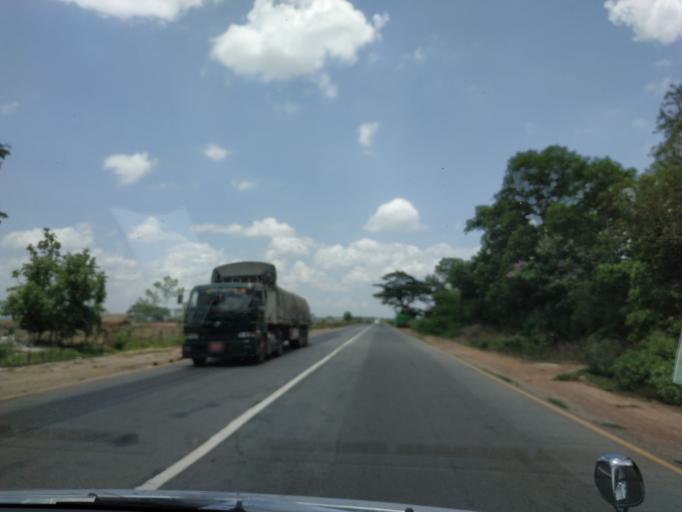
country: MM
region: Bago
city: Thanatpin
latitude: 17.4605
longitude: 96.5979
